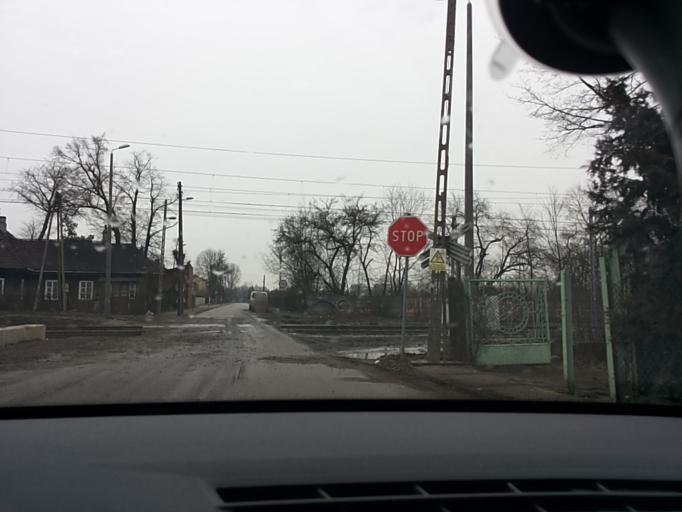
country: PL
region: Lodz Voivodeship
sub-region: Skierniewice
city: Skierniewice
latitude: 51.9633
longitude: 20.1354
